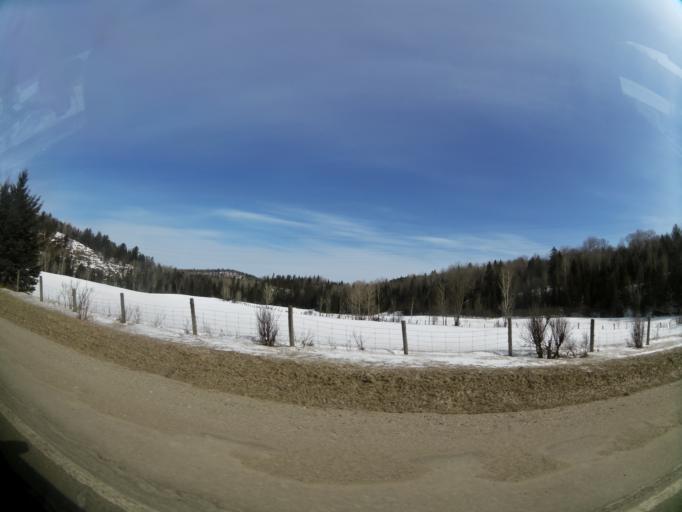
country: CA
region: Quebec
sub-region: Outaouais
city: Val-des-Monts
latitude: 45.7159
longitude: -75.5573
